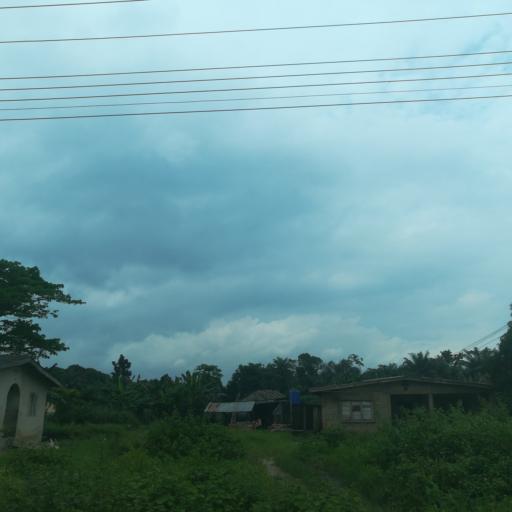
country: NG
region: Lagos
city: Ejirin
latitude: 6.6560
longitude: 3.7964
